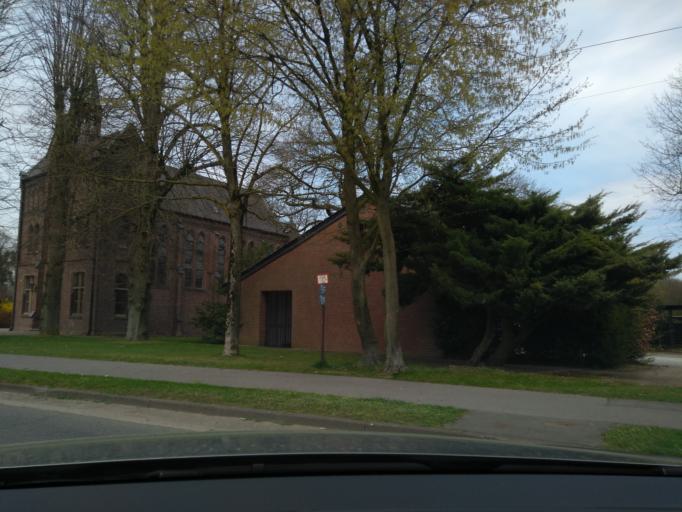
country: DE
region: North Rhine-Westphalia
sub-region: Regierungsbezirk Dusseldorf
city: Issum
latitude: 51.5785
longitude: 6.4577
